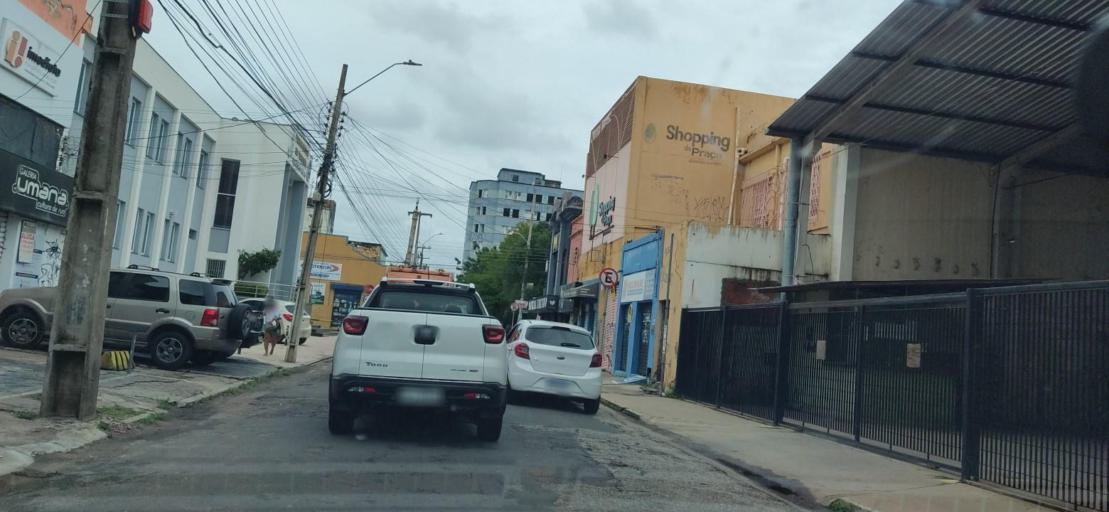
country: BR
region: Piaui
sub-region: Teresina
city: Teresina
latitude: -5.0891
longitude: -42.8125
